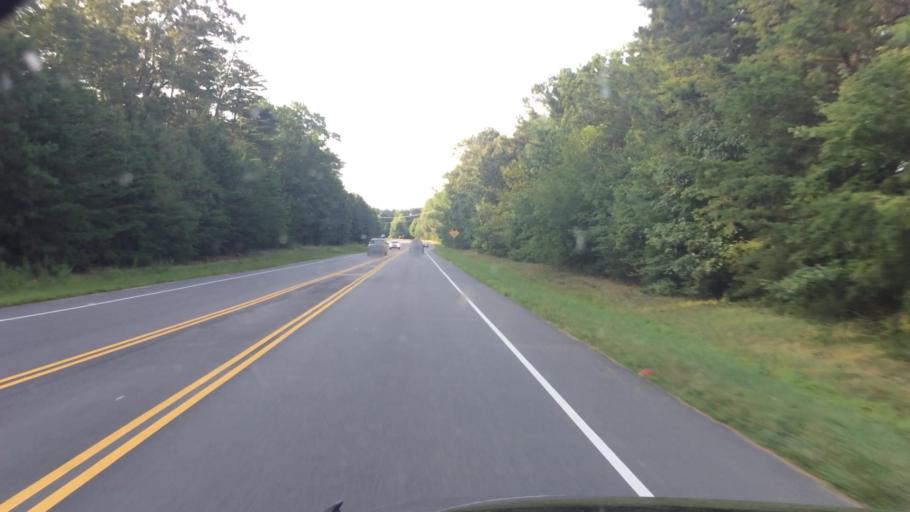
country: US
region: Virginia
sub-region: City of Williamsburg
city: Williamsburg
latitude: 37.2915
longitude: -76.7222
